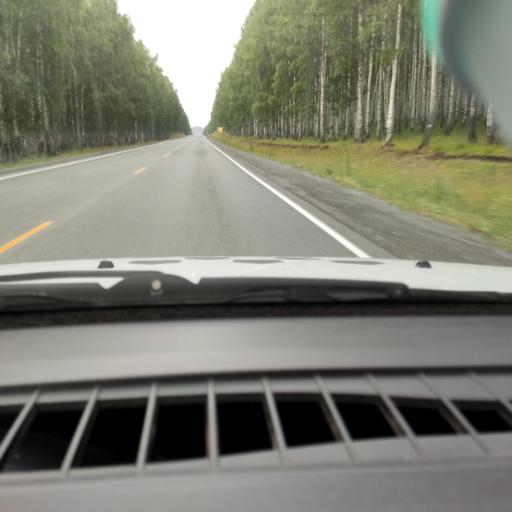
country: RU
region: Chelyabinsk
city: Karabash
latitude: 55.3269
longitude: 60.2288
